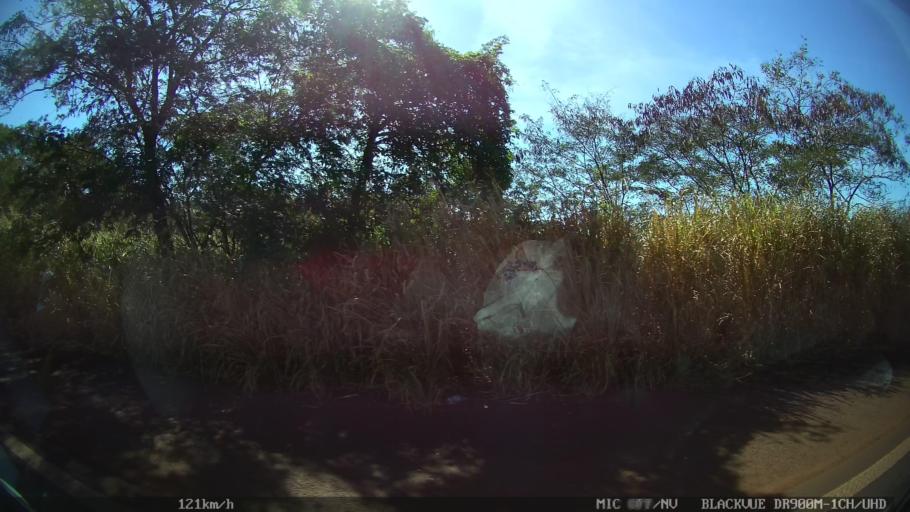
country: BR
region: Sao Paulo
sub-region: Guaira
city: Guaira
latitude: -20.4454
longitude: -48.4007
